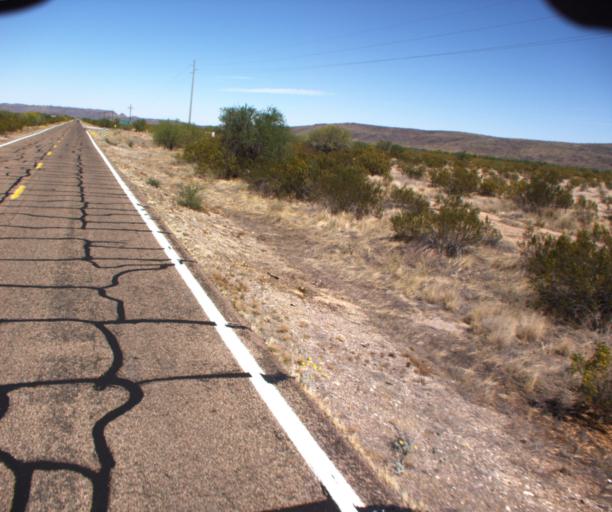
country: US
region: Arizona
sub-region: Pima County
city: Ajo
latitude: 32.4639
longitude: -112.8740
